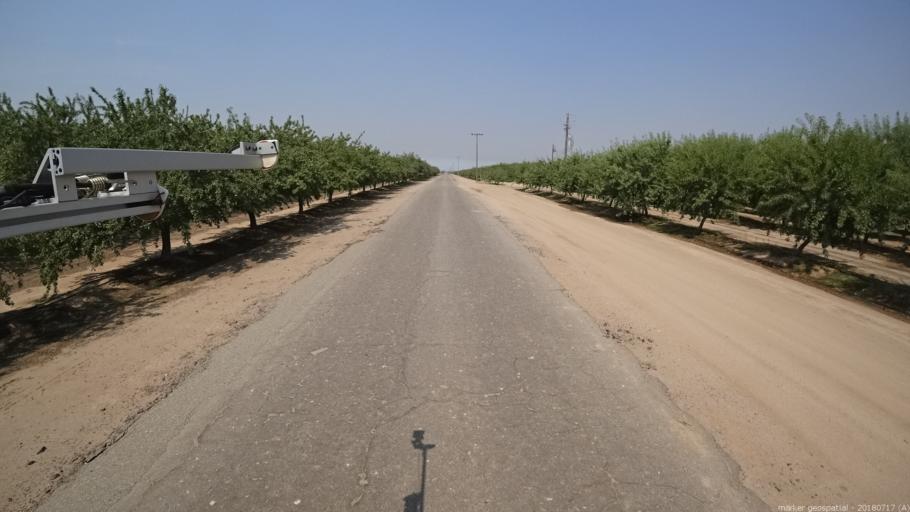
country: US
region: California
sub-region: Madera County
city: Fairmead
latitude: 37.1340
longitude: -120.1242
